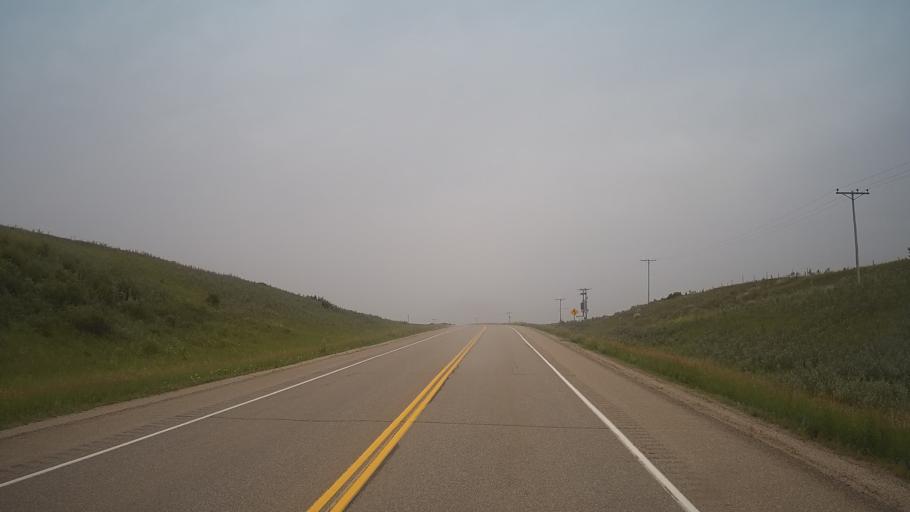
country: CA
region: Saskatchewan
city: Biggar
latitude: 52.0578
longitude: -107.8835
